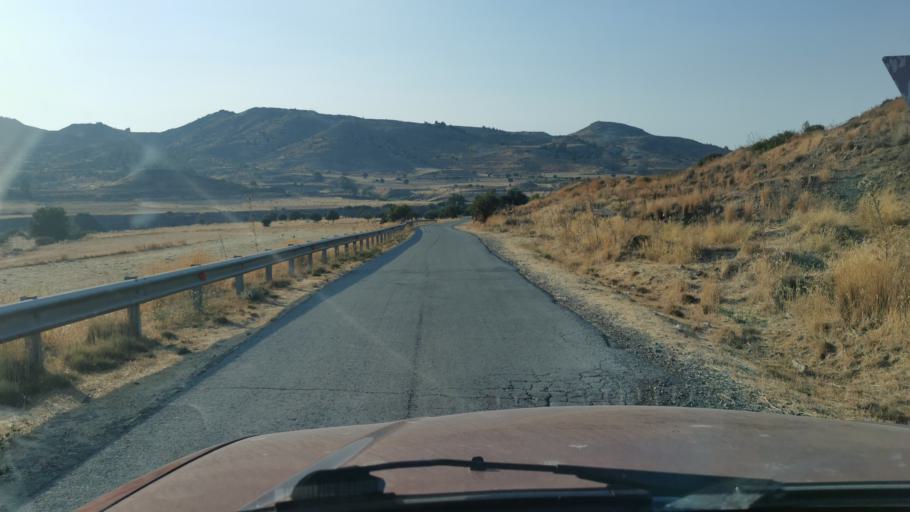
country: CY
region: Lefkosia
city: Peristerona
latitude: 35.0551
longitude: 33.0816
